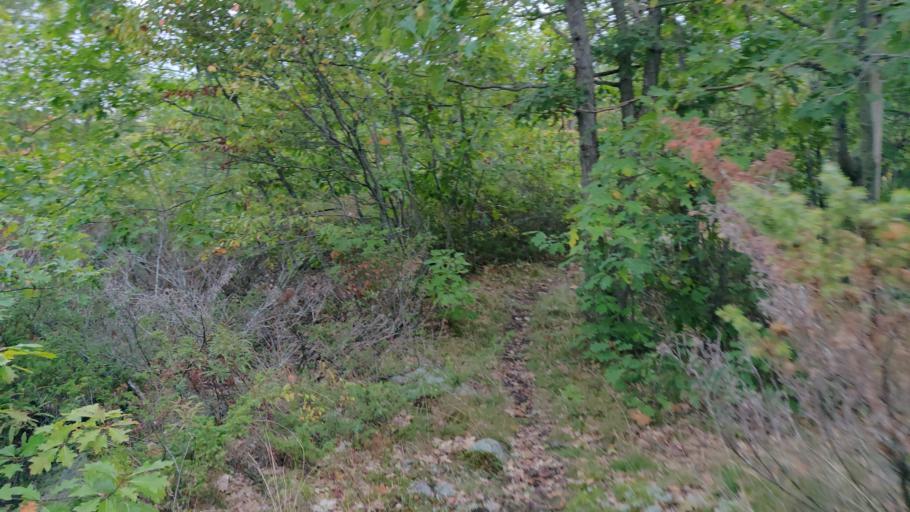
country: CA
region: Ontario
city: Greater Napanee
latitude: 44.5540
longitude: -77.1305
